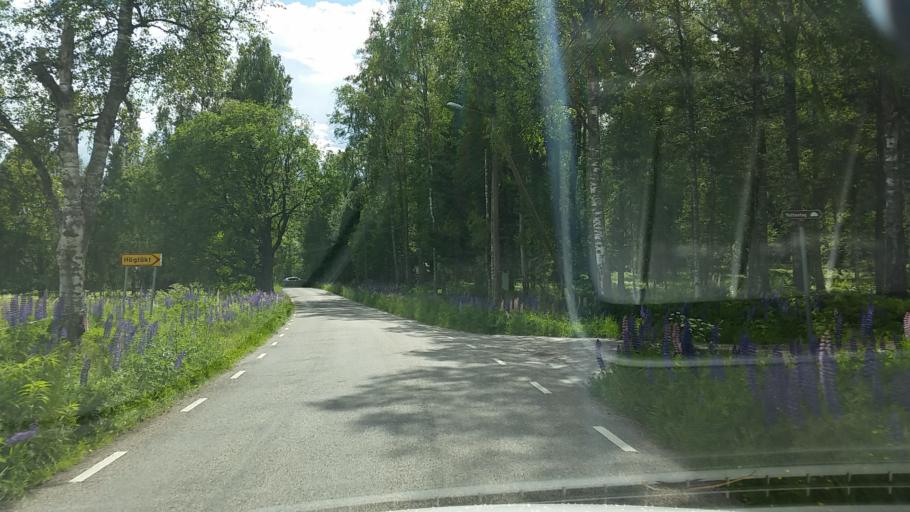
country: SE
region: Dalarna
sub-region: Faluns Kommun
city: Falun
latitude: 60.6281
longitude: 15.6551
